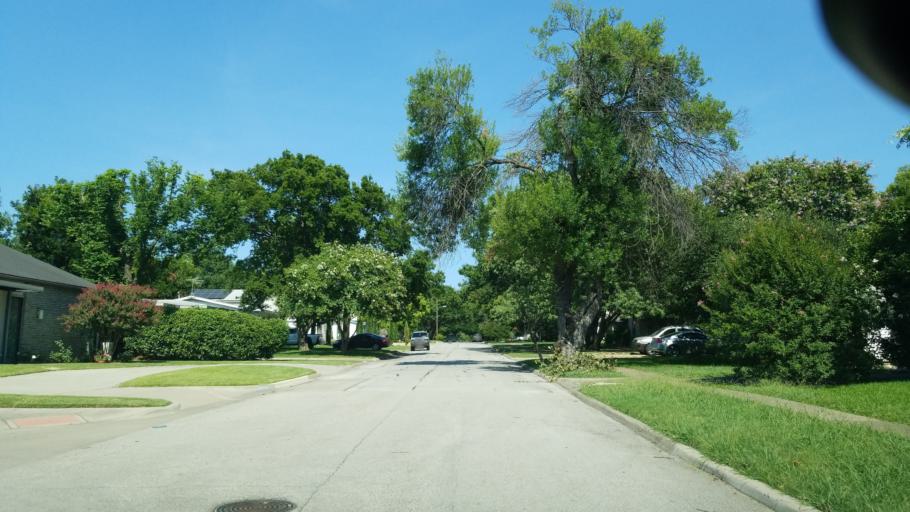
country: US
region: Texas
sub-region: Dallas County
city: Farmers Branch
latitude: 32.9195
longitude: -96.8912
